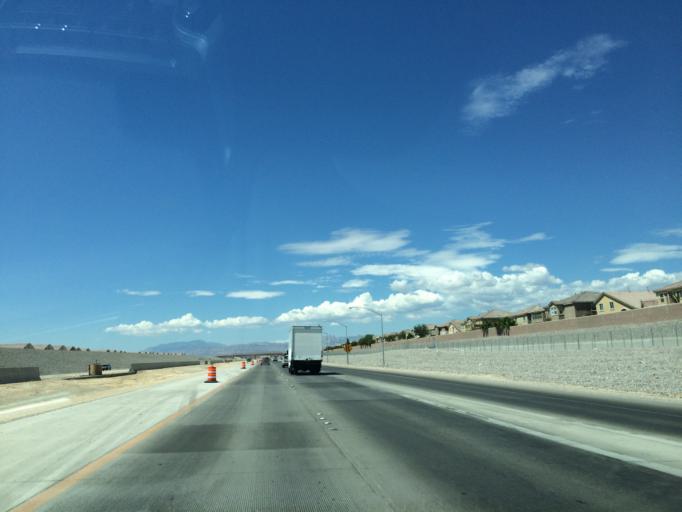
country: US
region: Nevada
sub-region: Clark County
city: North Las Vegas
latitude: 36.2875
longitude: -115.1835
